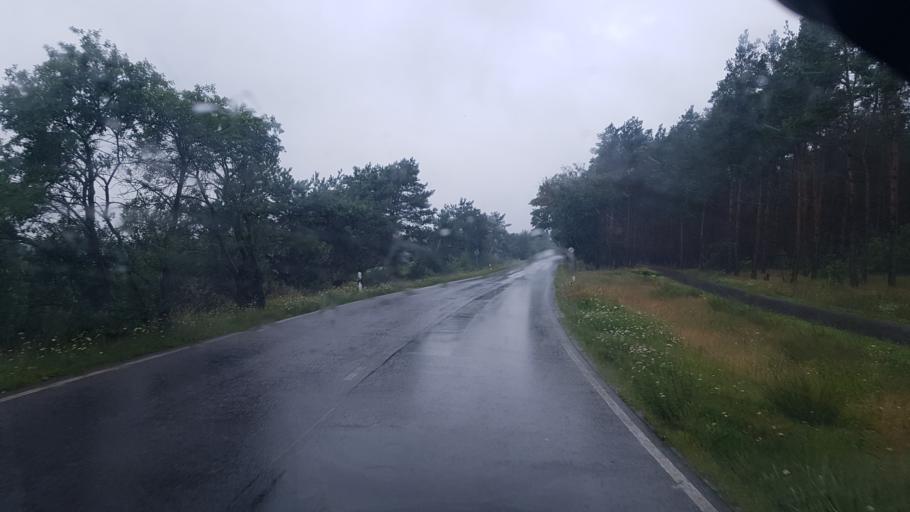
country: DE
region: Brandenburg
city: Golssen
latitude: 52.0501
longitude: 13.5900
